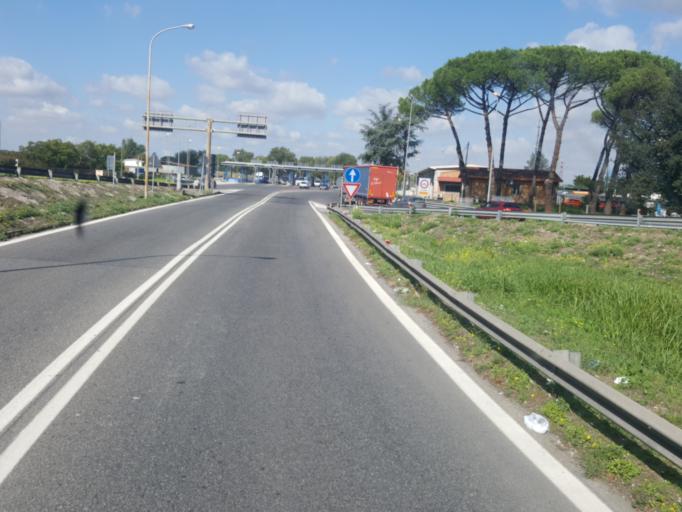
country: IT
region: Campania
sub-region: Provincia di Napoli
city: Cimitile
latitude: 40.9363
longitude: 14.4991
